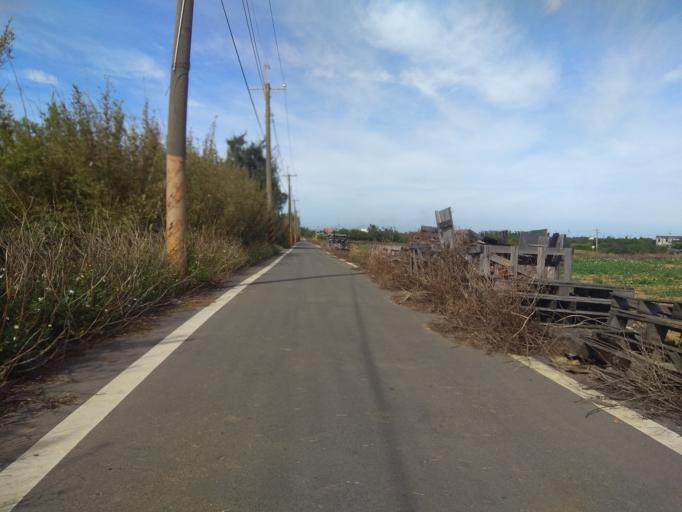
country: TW
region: Taiwan
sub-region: Hsinchu
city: Zhubei
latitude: 25.0121
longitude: 121.0788
